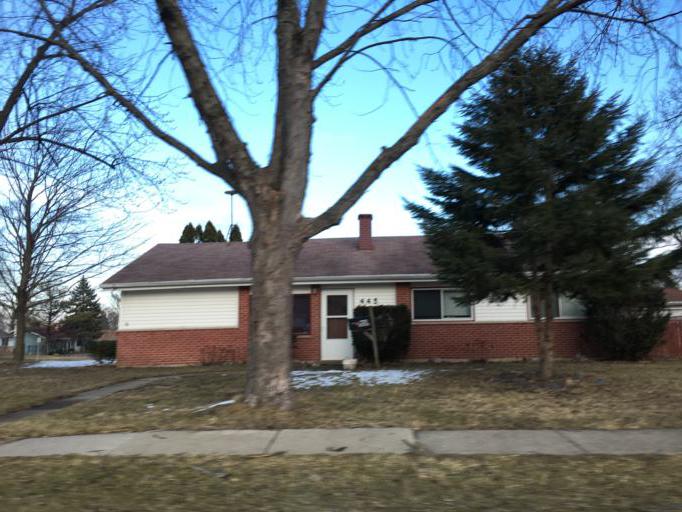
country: US
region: Illinois
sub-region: Cook County
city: Schaumburg
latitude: 42.0351
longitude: -88.0833
